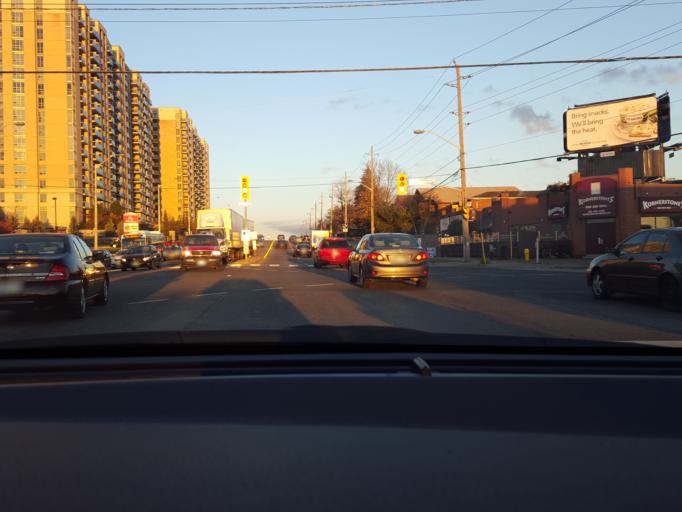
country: CA
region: Ontario
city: Scarborough
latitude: 43.7633
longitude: -79.2917
